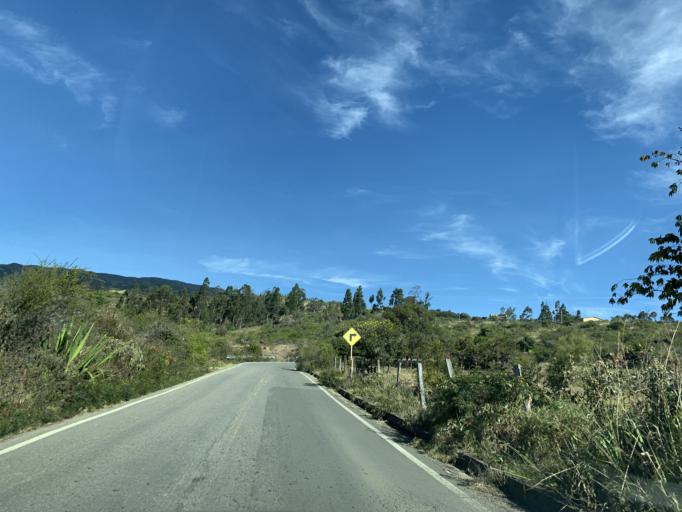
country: CO
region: Boyaca
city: Santa Sofia
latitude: 5.6865
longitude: -73.5880
